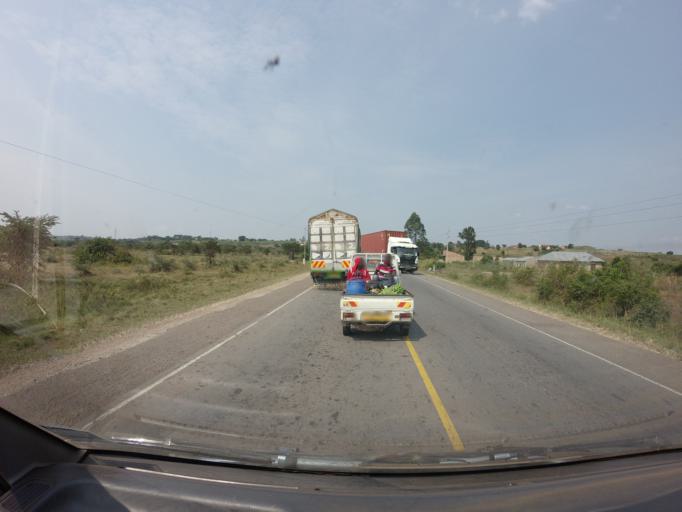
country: UG
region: Central Region
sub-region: Lwengo District
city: Lwengo
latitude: -0.4041
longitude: 31.3747
